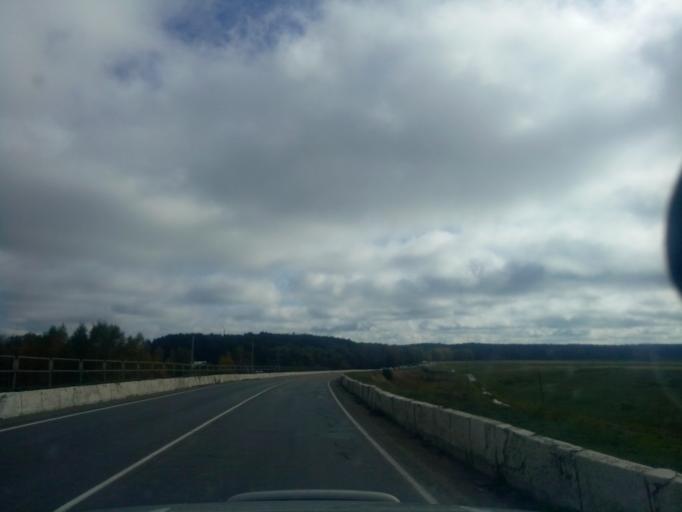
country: BY
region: Minsk
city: Zaslawye
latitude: 53.9988
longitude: 27.2853
